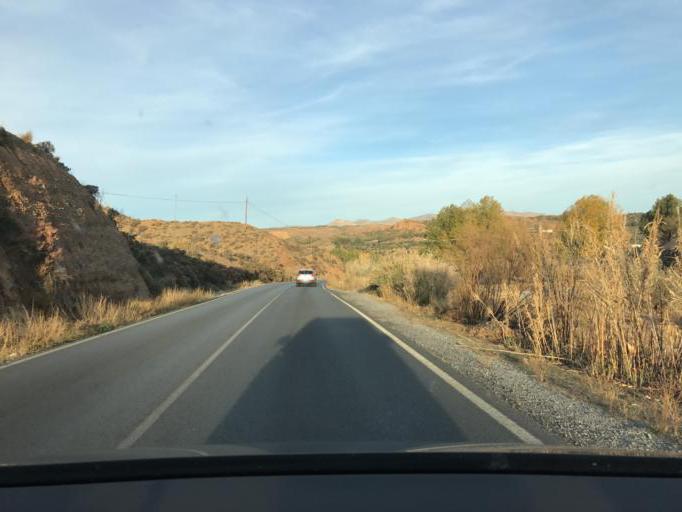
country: ES
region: Andalusia
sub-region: Provincia de Granada
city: Guadix
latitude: 37.2852
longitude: -3.1242
